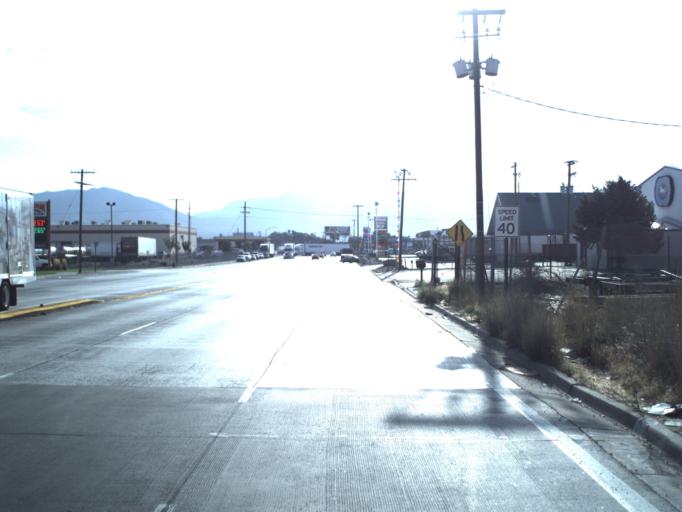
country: US
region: Utah
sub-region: Salt Lake County
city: Salt Lake City
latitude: 40.7404
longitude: -111.9484
